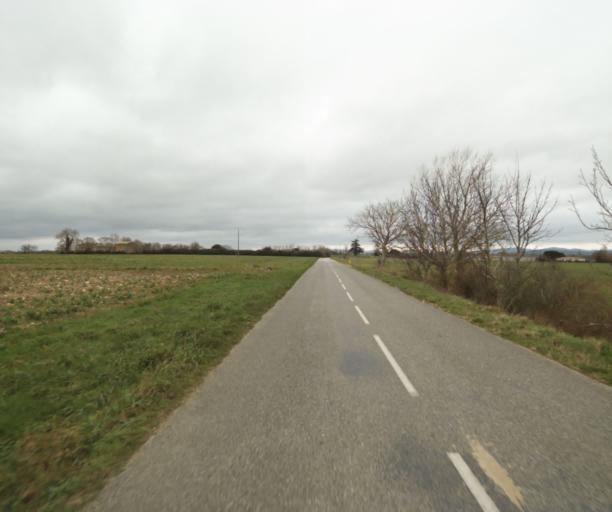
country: FR
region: Midi-Pyrenees
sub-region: Departement de l'Ariege
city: Pamiers
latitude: 43.1691
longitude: 1.6351
